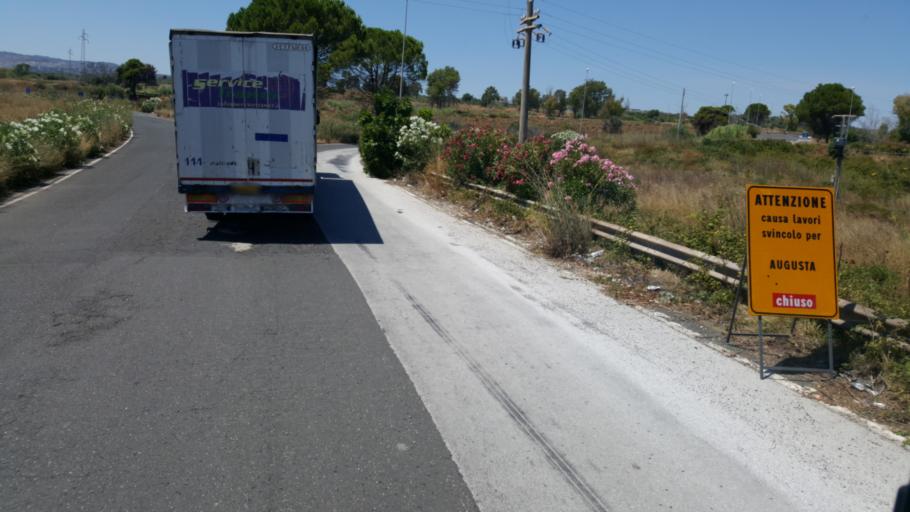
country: IT
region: Sicily
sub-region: Provincia di Siracusa
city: Melilli
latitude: 37.2183
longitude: 15.1555
